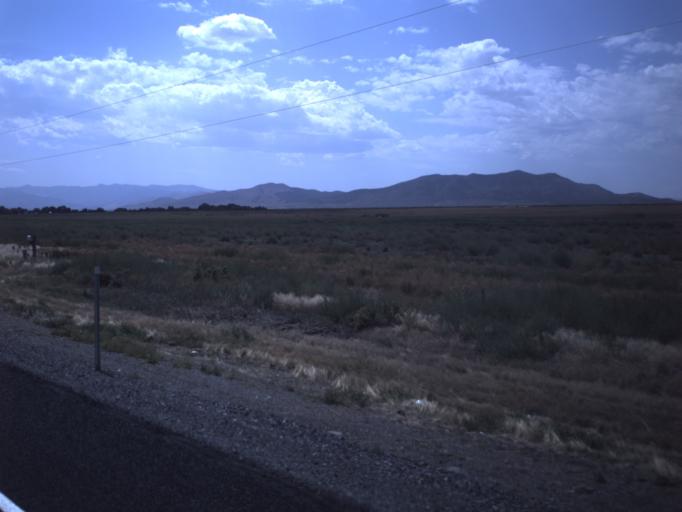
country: US
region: Utah
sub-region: Utah County
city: Eagle Mountain
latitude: 40.2752
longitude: -112.0944
